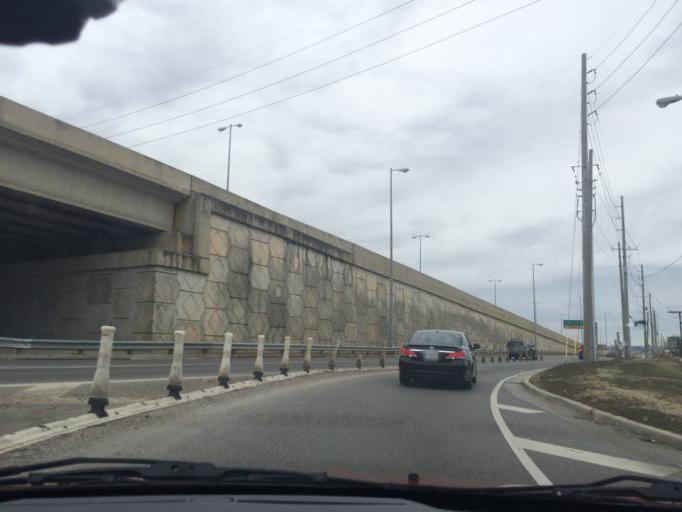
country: US
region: Alabama
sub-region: Madison County
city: Huntsville
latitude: 34.6909
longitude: -86.5804
